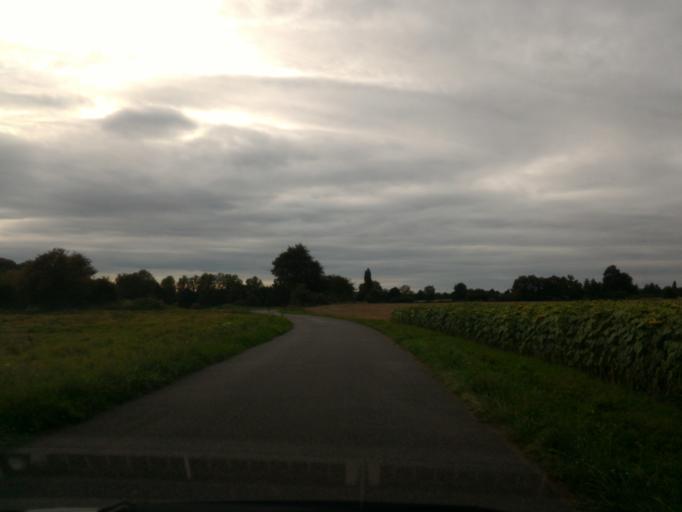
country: FR
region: Poitou-Charentes
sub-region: Departement de la Charente
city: Brigueuil
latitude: 45.9271
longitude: 0.8324
